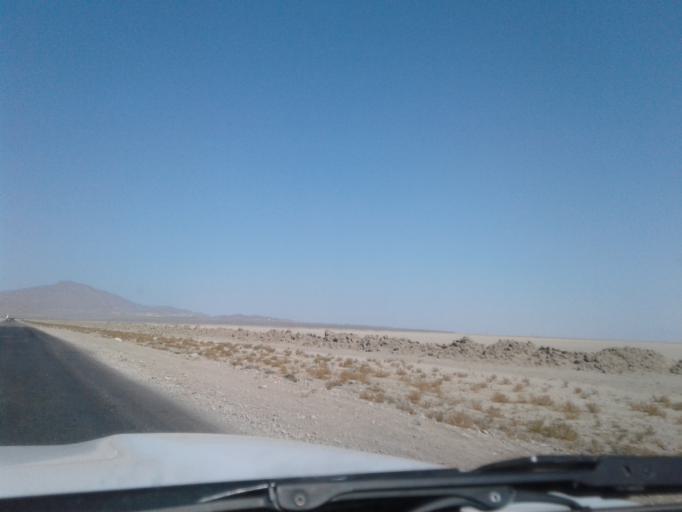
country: TM
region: Balkan
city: Gumdag
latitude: 39.2350
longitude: 54.6943
